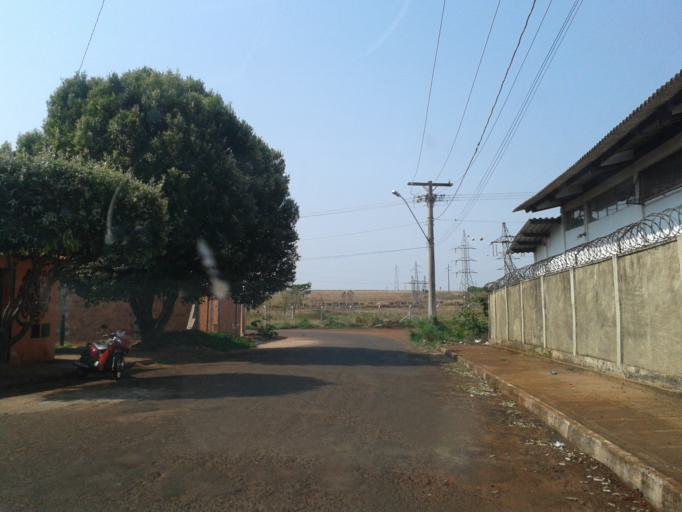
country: BR
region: Minas Gerais
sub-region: Ituiutaba
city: Ituiutaba
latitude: -18.9627
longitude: -49.4489
